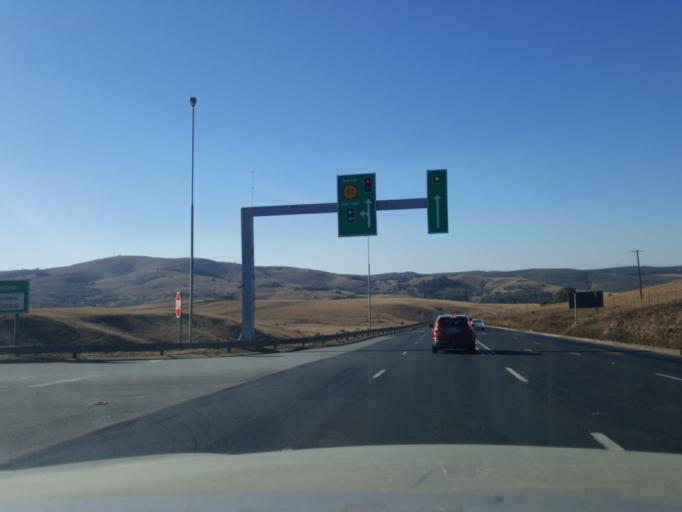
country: ZA
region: Mpumalanga
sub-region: Nkangala District Municipality
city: Belfast
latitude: -25.6198
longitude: 30.2641
